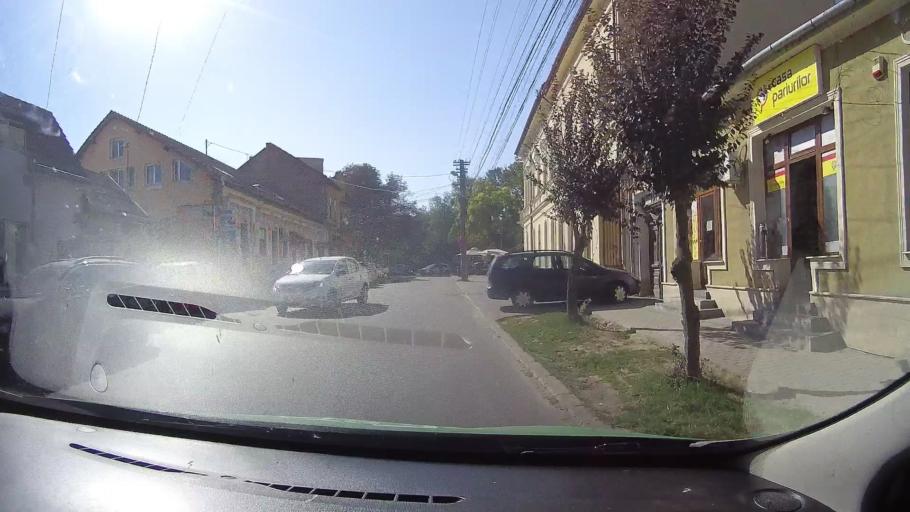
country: RO
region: Satu Mare
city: Carei
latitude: 47.6847
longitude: 22.4697
